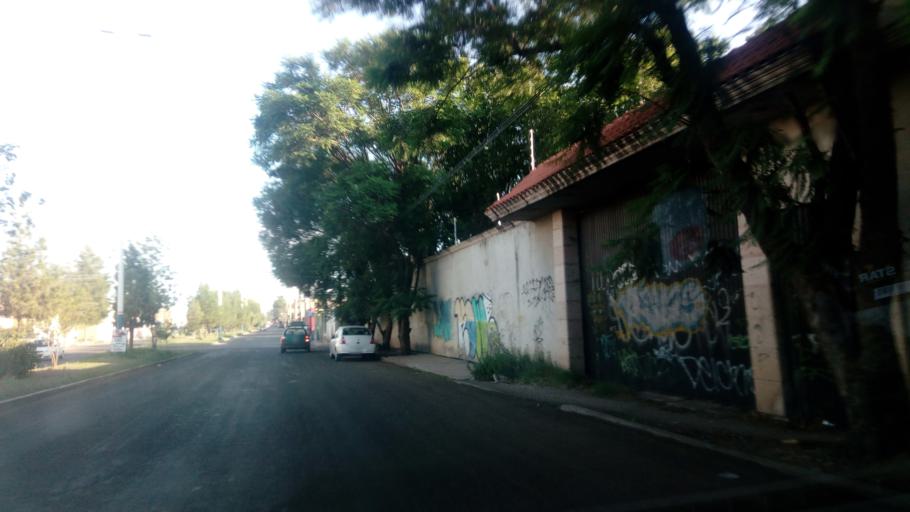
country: MX
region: Durango
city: Victoria de Durango
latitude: 24.0425
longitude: -104.6113
